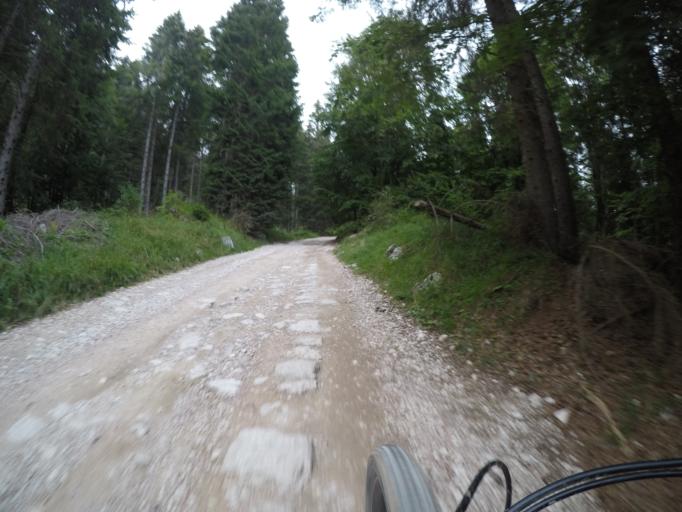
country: IT
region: Veneto
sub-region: Provincia di Vicenza
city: Gallio
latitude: 45.9118
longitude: 11.5243
